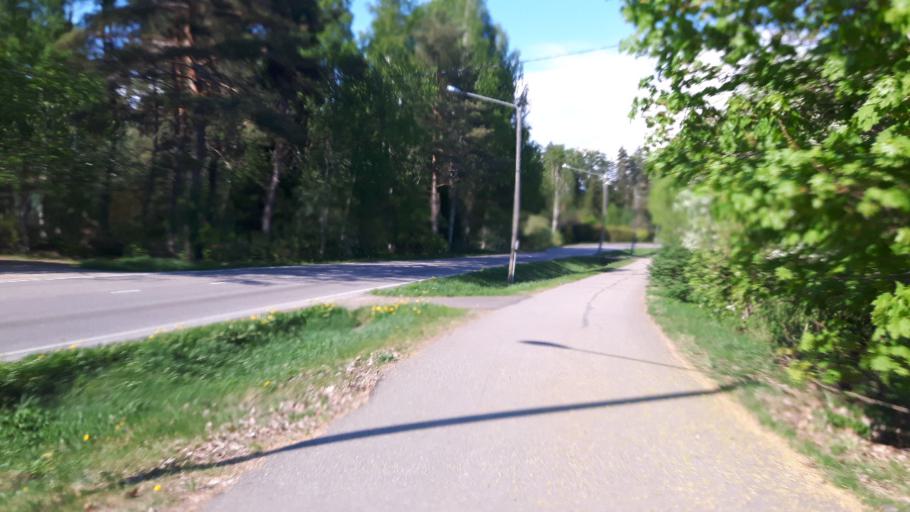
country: FI
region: Kymenlaakso
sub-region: Kotka-Hamina
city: Broby
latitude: 60.4925
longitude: 26.7688
